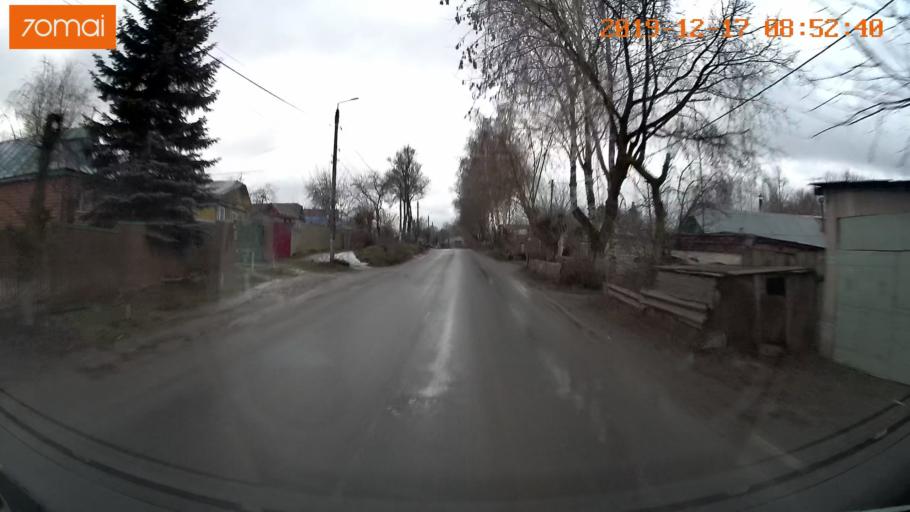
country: RU
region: Vladimir
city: Kosterevo
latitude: 55.9466
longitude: 39.6322
